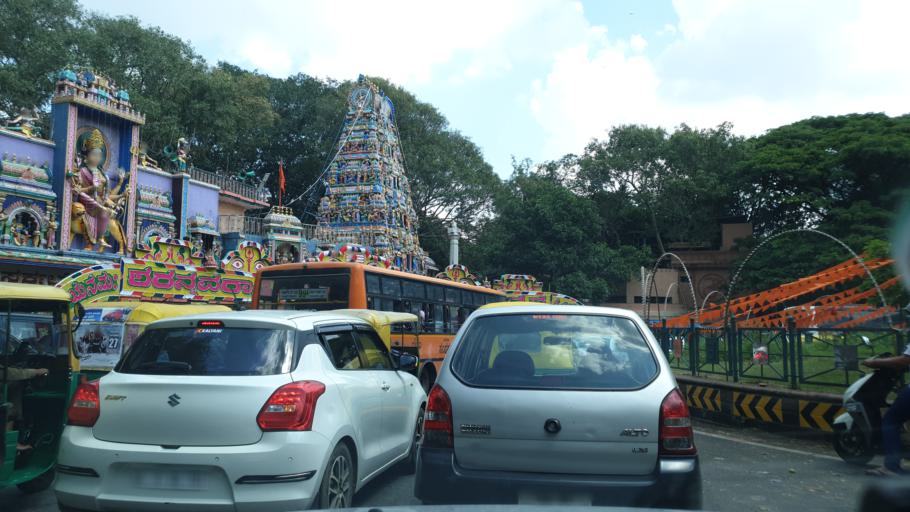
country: IN
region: Karnataka
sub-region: Bangalore Urban
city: Bangalore
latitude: 13.0122
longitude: 77.5690
